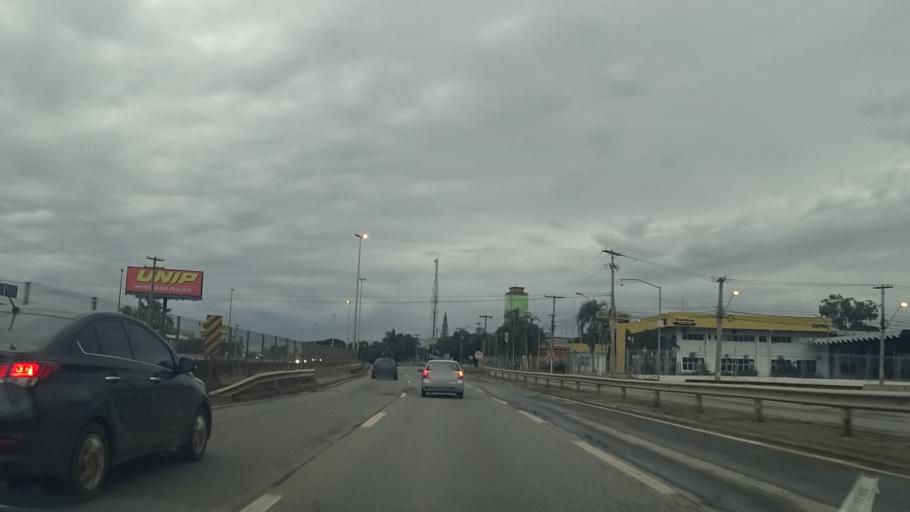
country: BR
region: Goias
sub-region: Goiania
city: Goiania
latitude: -16.7176
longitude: -49.2373
